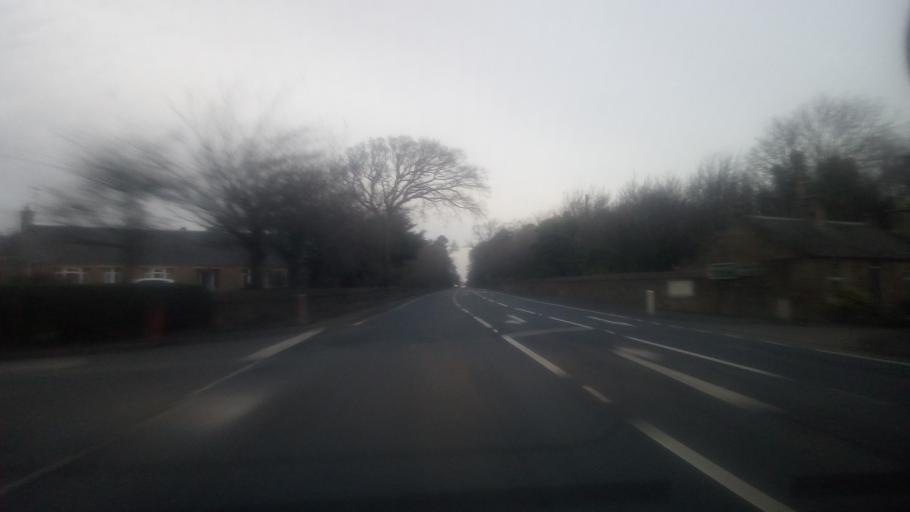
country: GB
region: Scotland
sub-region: Fife
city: Pathhead
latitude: 55.8774
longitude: -2.9859
